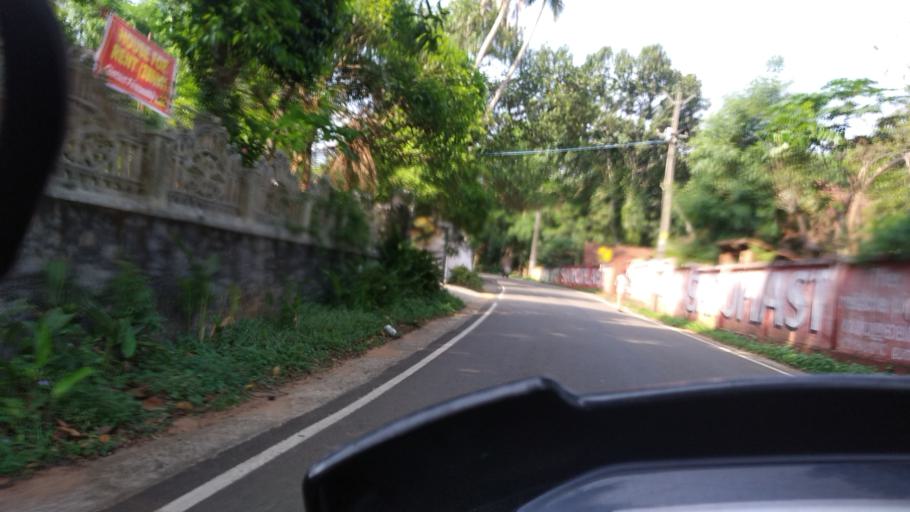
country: IN
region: Kerala
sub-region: Ernakulam
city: Piravam
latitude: 9.8487
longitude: 76.5345
